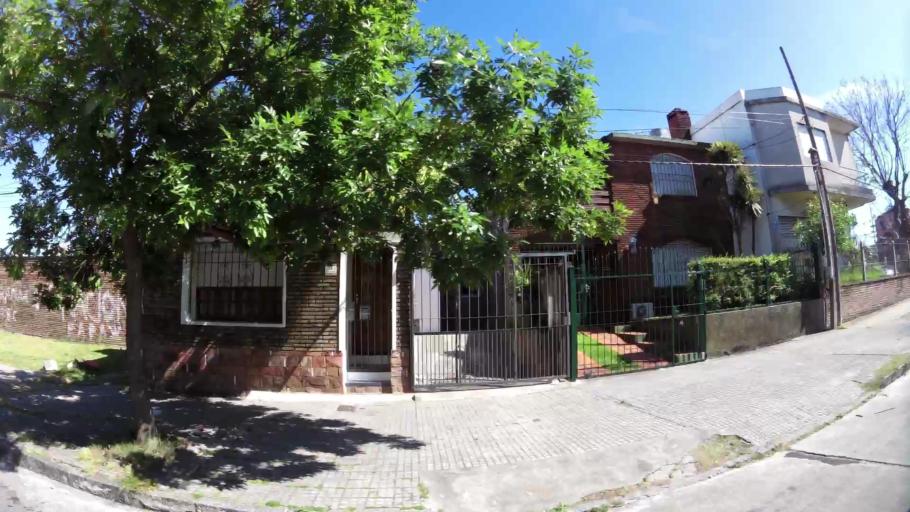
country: UY
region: Montevideo
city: Montevideo
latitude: -34.8883
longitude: -56.1417
